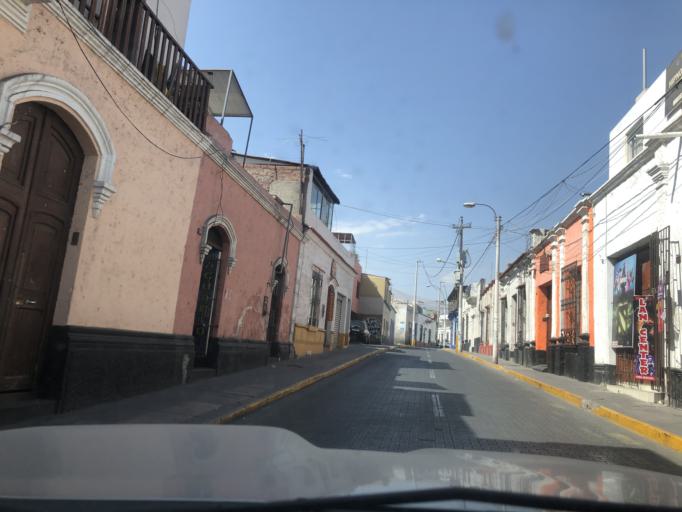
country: PE
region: Arequipa
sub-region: Provincia de Arequipa
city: Arequipa
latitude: -16.3950
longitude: -71.5323
